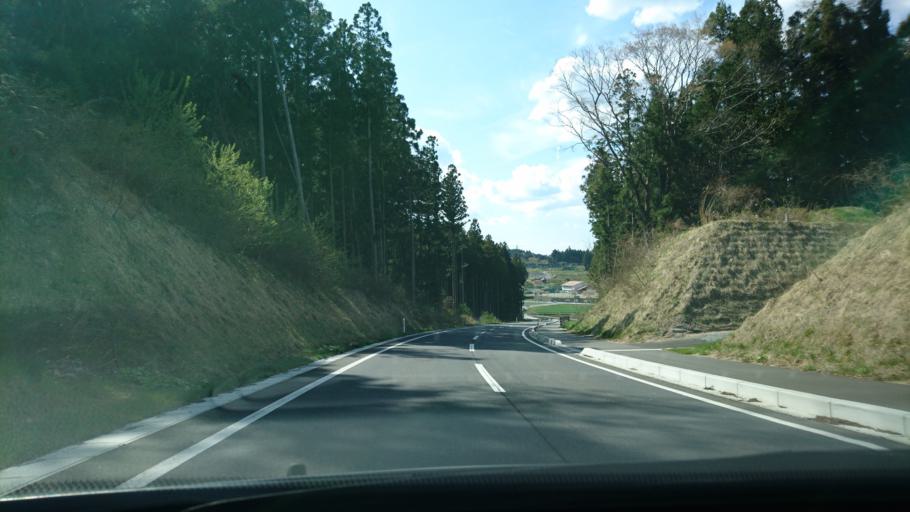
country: JP
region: Iwate
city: Ichinoseki
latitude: 38.9295
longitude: 141.4297
